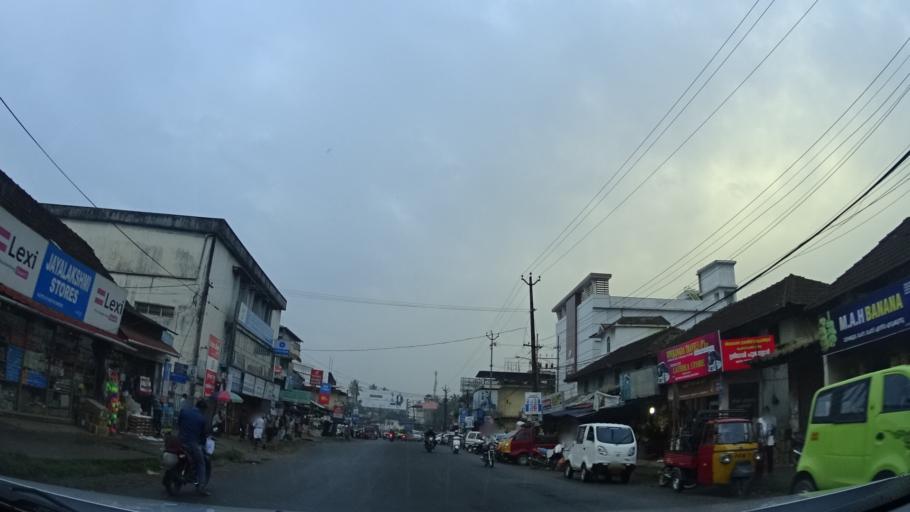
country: IN
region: Kerala
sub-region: Wayanad
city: Kalpetta
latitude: 11.6080
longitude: 76.0835
